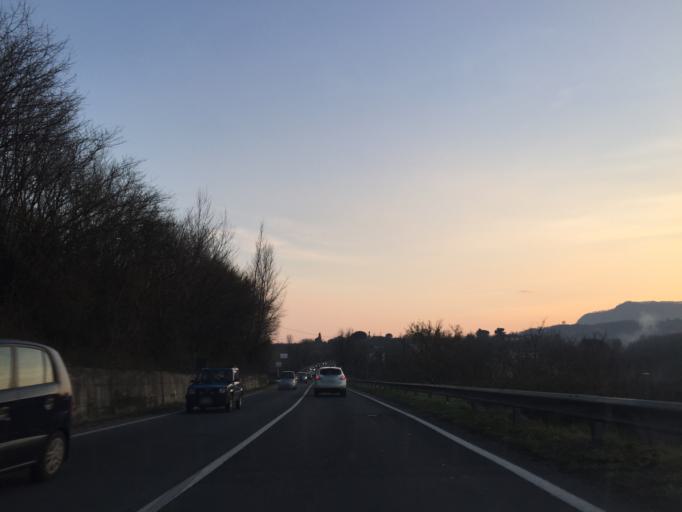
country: IT
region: Campania
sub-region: Provincia di Avellino
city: Avellino
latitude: 40.9083
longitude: 14.8104
